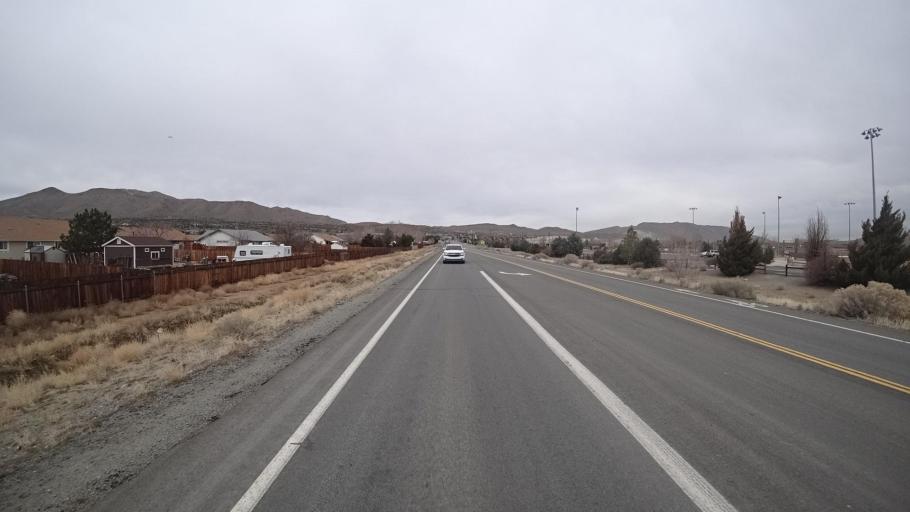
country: US
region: Nevada
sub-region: Washoe County
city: Spanish Springs
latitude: 39.6447
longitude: -119.7222
